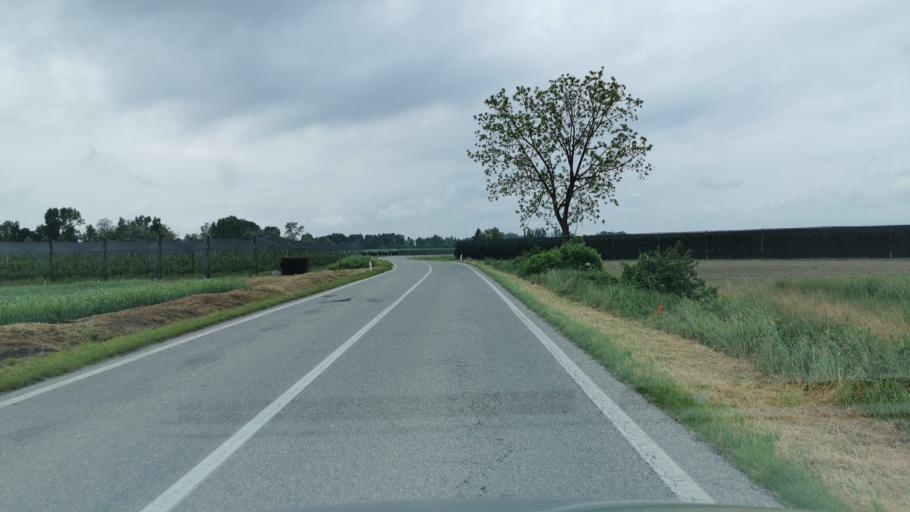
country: IT
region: Piedmont
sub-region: Provincia di Cuneo
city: Savigliano
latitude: 44.6185
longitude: 7.6299
